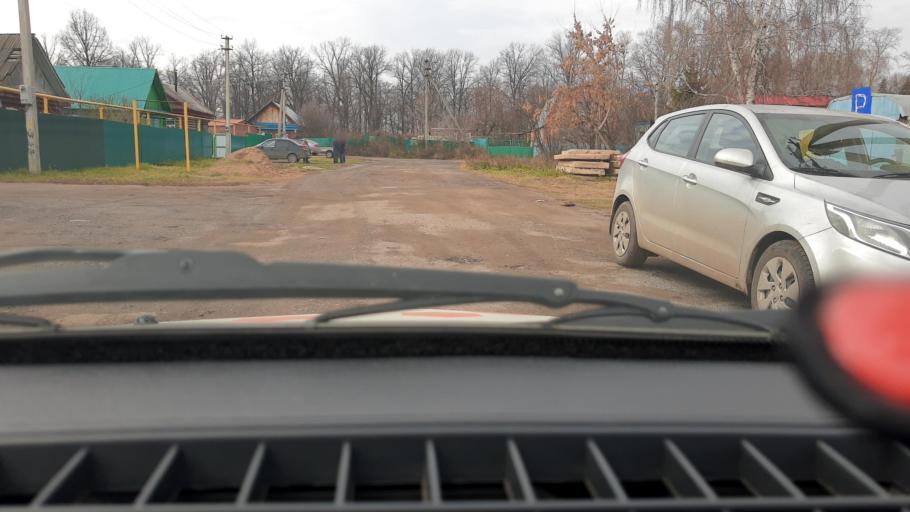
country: RU
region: Bashkortostan
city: Mikhaylovka
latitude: 54.7945
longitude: 55.9392
